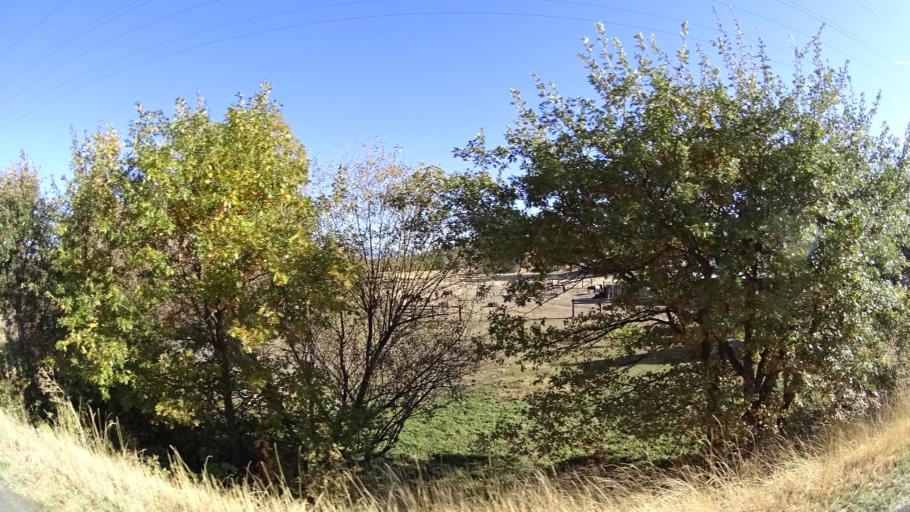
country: US
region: California
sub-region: Siskiyou County
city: Yreka
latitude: 41.4610
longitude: -122.8876
